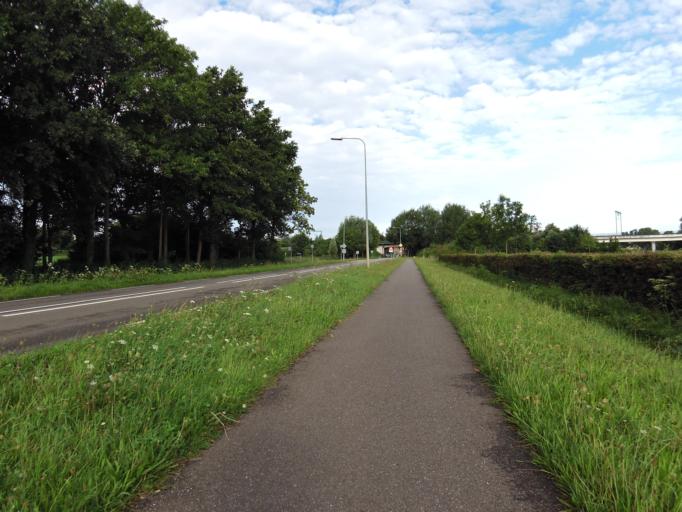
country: NL
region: Limburg
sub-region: Gemeente Voerendaal
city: Voerendaal
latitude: 50.8779
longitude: 5.9105
